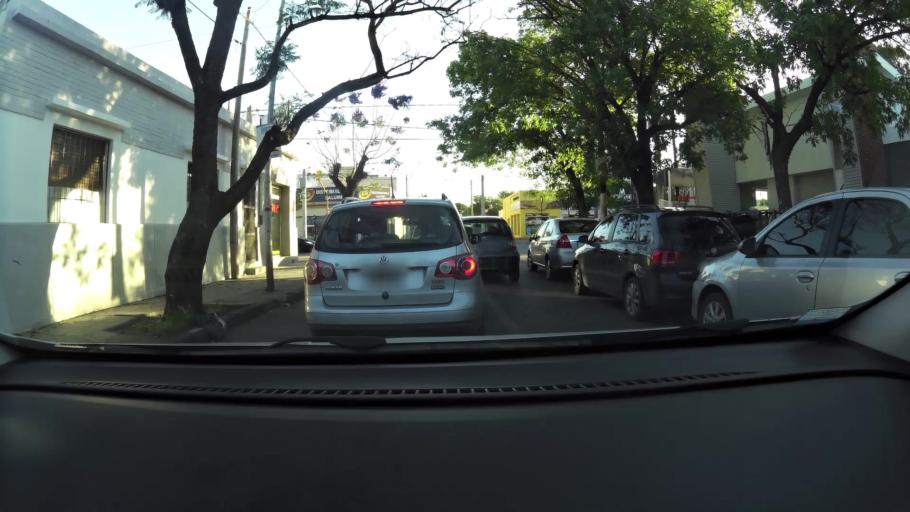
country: AR
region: Cordoba
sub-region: Departamento de Capital
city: Cordoba
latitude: -31.3860
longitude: -64.2177
